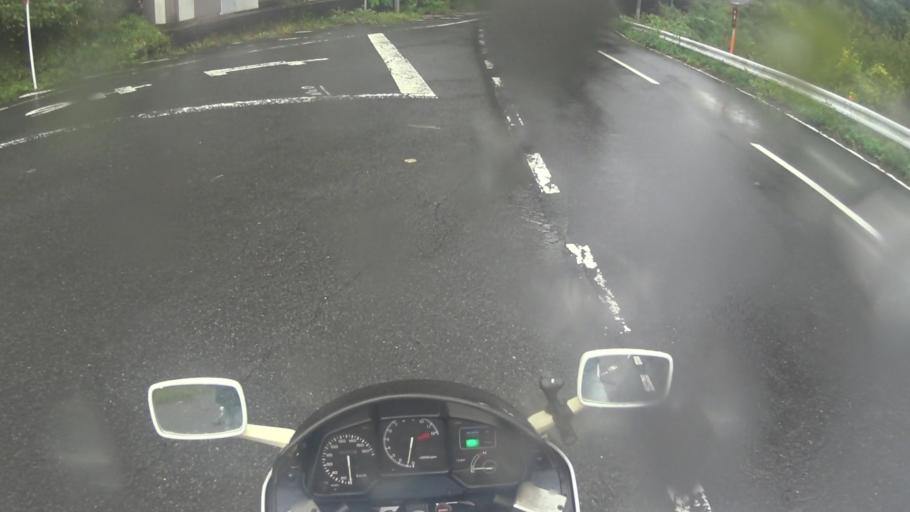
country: JP
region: Kyoto
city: Miyazu
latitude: 35.4934
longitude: 135.1666
